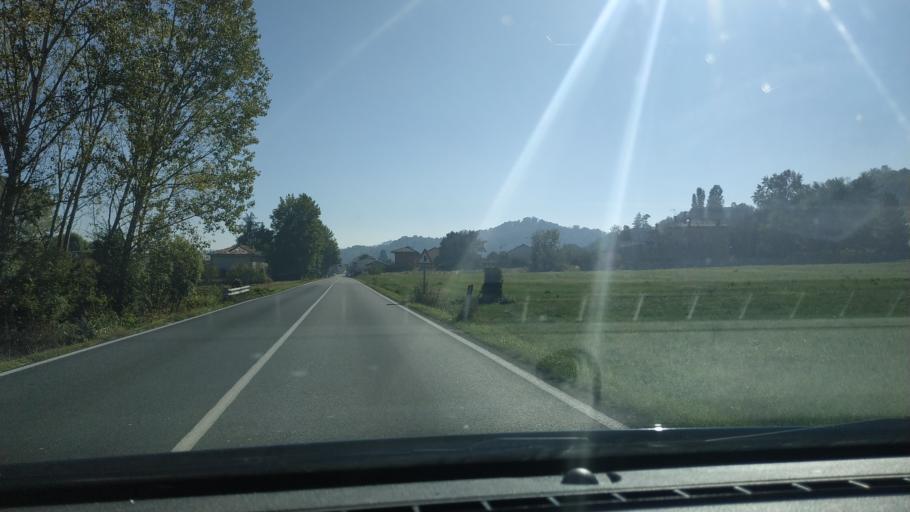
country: IT
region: Piedmont
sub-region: Provincia di Torino
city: Pomaretto
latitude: 45.1574
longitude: 8.0393
